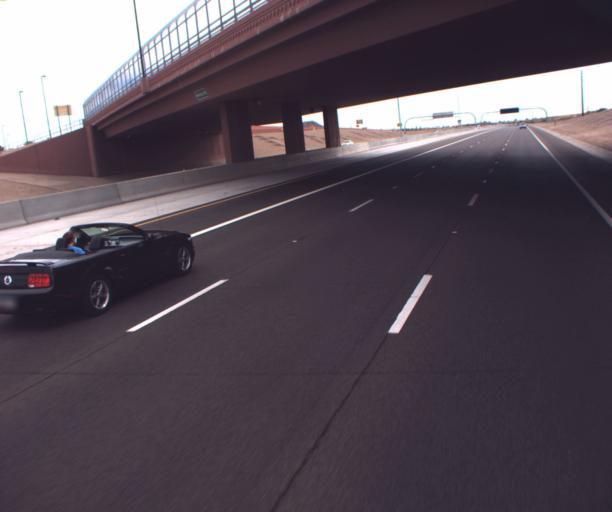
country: US
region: Arizona
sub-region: Pinal County
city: Apache Junction
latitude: 33.4517
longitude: -111.6703
